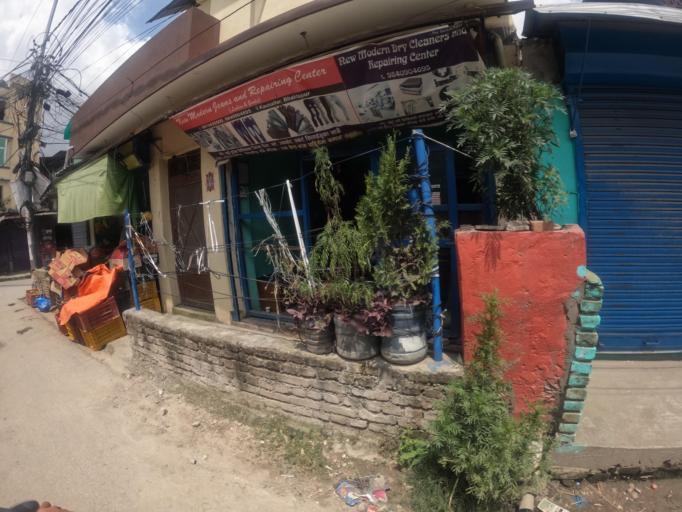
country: NP
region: Central Region
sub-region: Bagmati Zone
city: Patan
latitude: 27.6755
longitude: 85.3659
